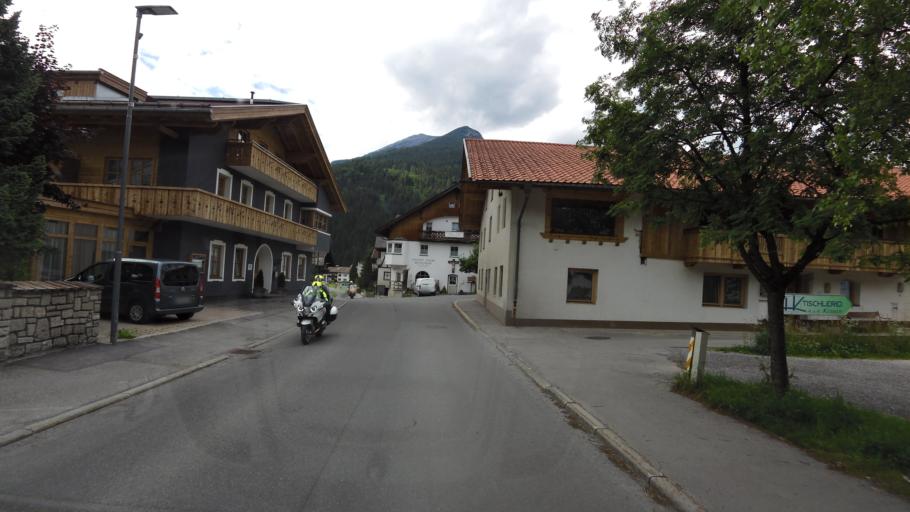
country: AT
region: Tyrol
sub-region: Politischer Bezirk Reutte
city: Ehrwald
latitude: 47.4062
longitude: 10.9171
